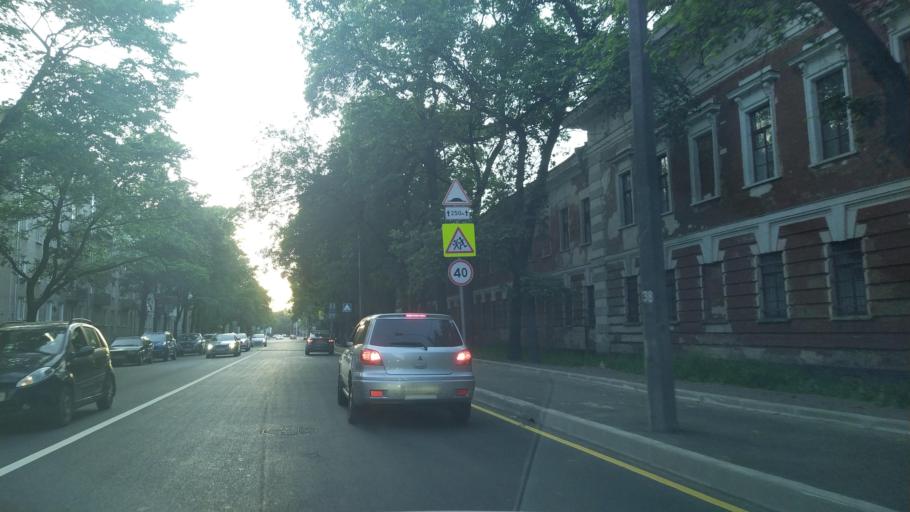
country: RU
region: St.-Petersburg
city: Kronshtadt
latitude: 59.9990
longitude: 29.7732
